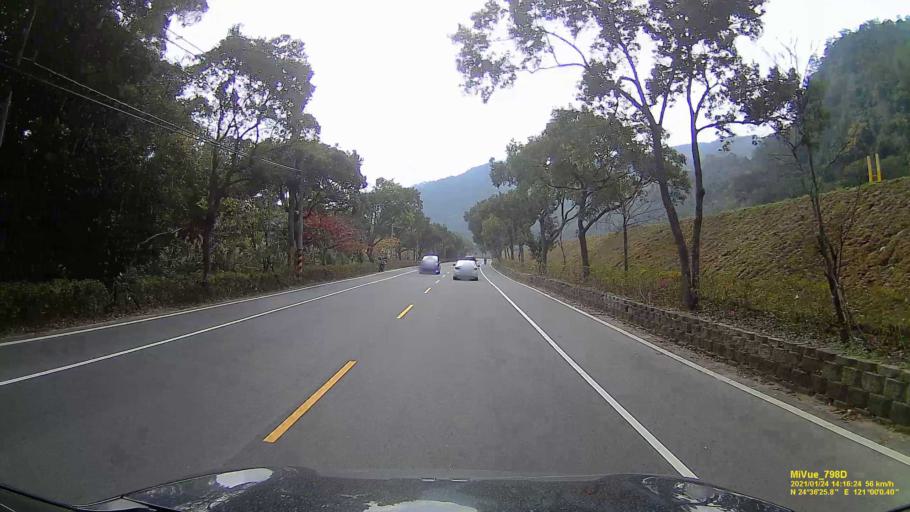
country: TW
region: Taiwan
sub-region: Miaoli
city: Miaoli
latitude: 24.6069
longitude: 120.9999
